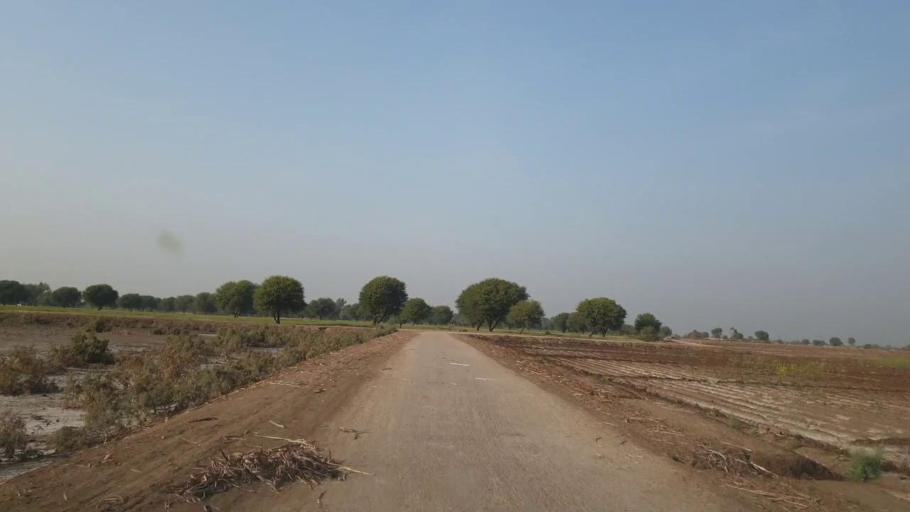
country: PK
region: Sindh
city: Pithoro
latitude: 25.6729
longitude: 69.2036
